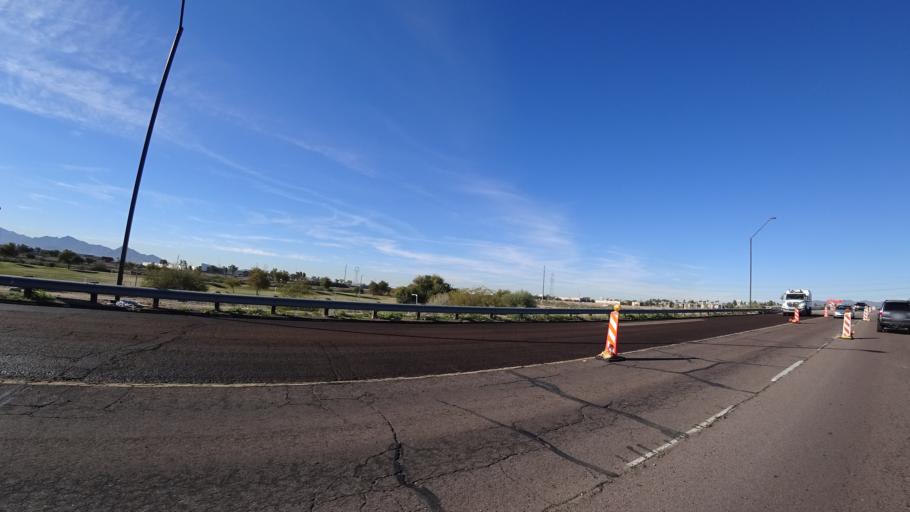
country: US
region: Arizona
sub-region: Maricopa County
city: Avondale
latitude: 33.4618
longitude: -112.3273
